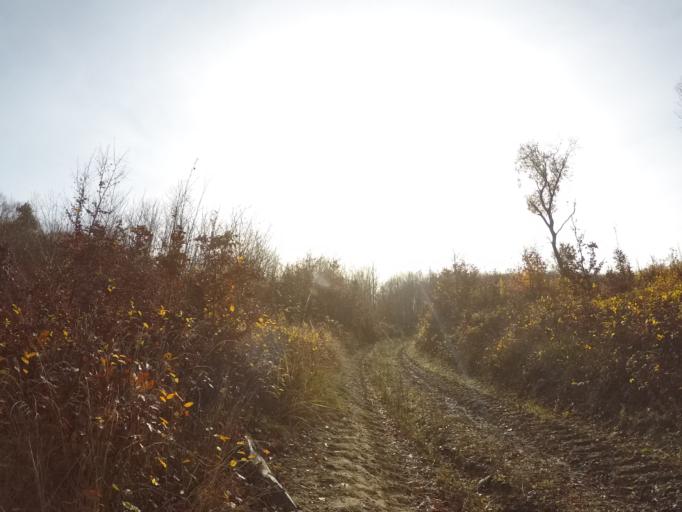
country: SK
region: Presovsky
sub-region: Okres Presov
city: Presov
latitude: 48.9176
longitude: 21.2117
